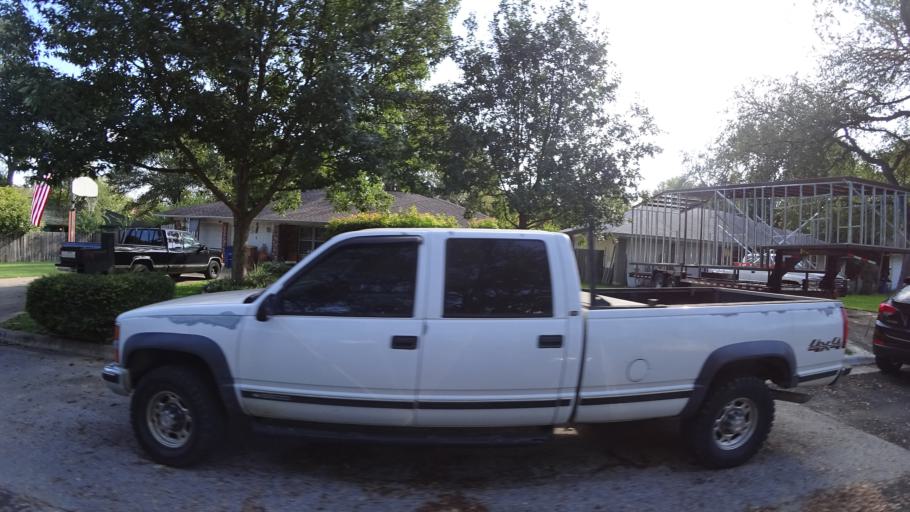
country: US
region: Texas
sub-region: Travis County
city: Rollingwood
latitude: 30.2120
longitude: -97.8081
